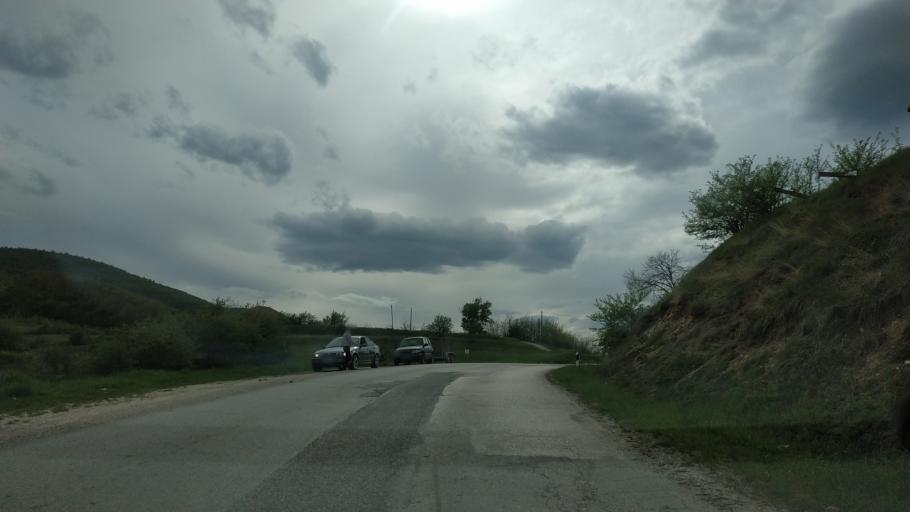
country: RS
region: Central Serbia
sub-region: Zajecarski Okrug
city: Soko Banja
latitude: 43.6434
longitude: 21.8936
